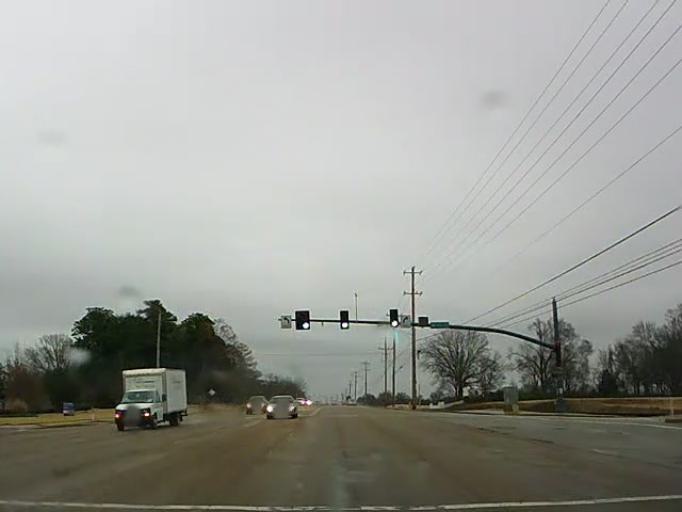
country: US
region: Tennessee
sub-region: Shelby County
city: Collierville
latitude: 35.0472
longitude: -89.7117
